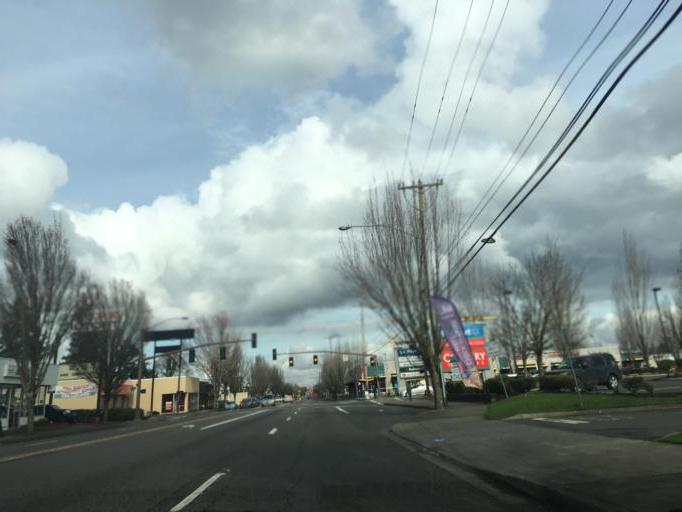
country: US
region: Oregon
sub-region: Multnomah County
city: Lents
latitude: 45.4913
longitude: -122.5787
